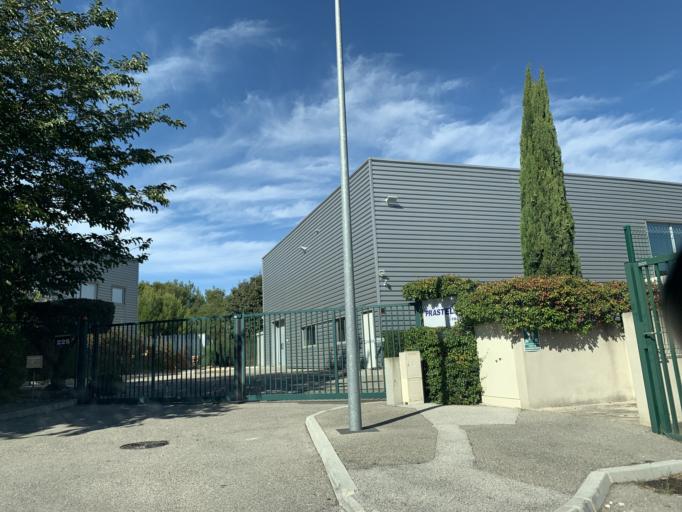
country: FR
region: Provence-Alpes-Cote d'Azur
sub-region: Departement des Bouches-du-Rhone
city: La Ciotat
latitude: 43.2023
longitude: 5.6009
